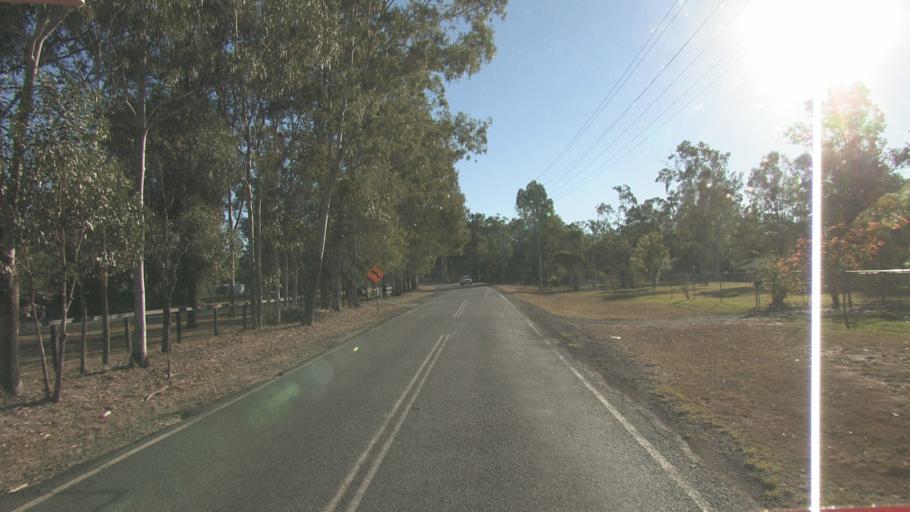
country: AU
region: Queensland
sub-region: Logan
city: North Maclean
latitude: -27.7578
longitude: 153.0307
